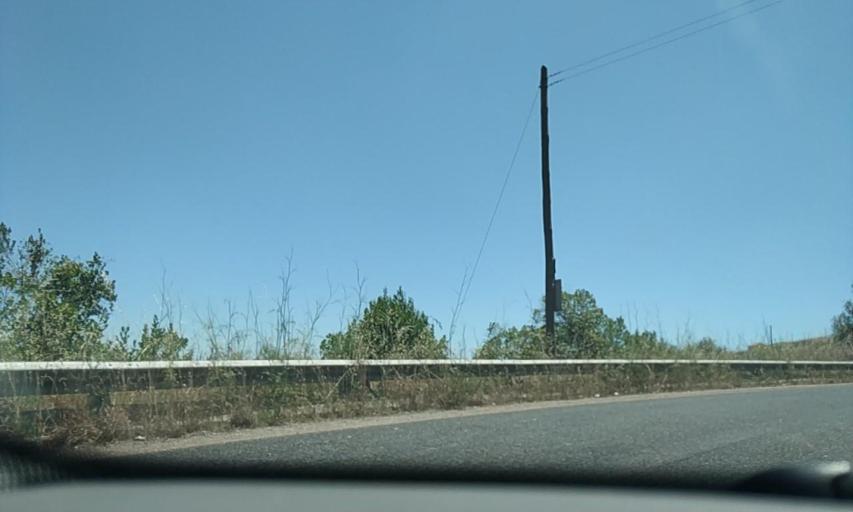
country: PT
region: Lisbon
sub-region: Odivelas
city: Canecas
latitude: 38.8605
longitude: -9.2095
